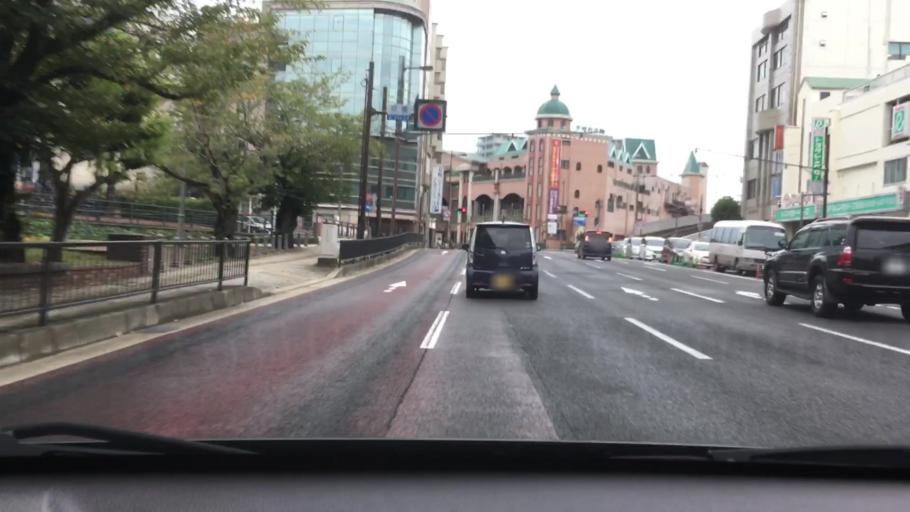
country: JP
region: Nagasaki
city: Nagasaki-shi
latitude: 32.7727
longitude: 129.8628
